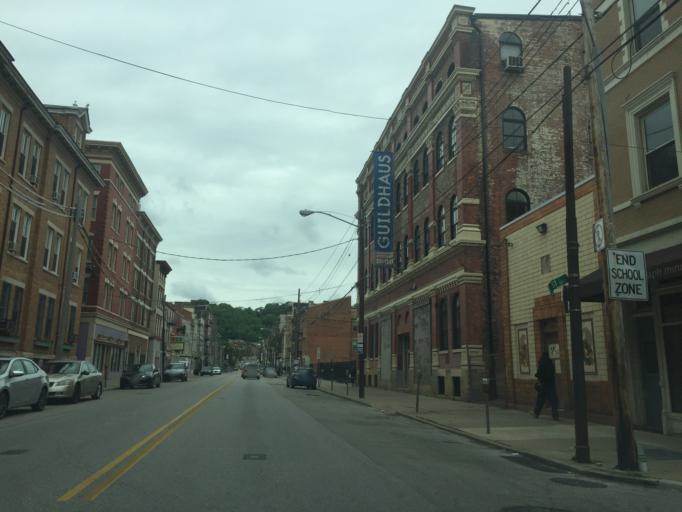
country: US
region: Kentucky
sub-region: Campbell County
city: Newport
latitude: 39.1134
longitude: -84.5160
